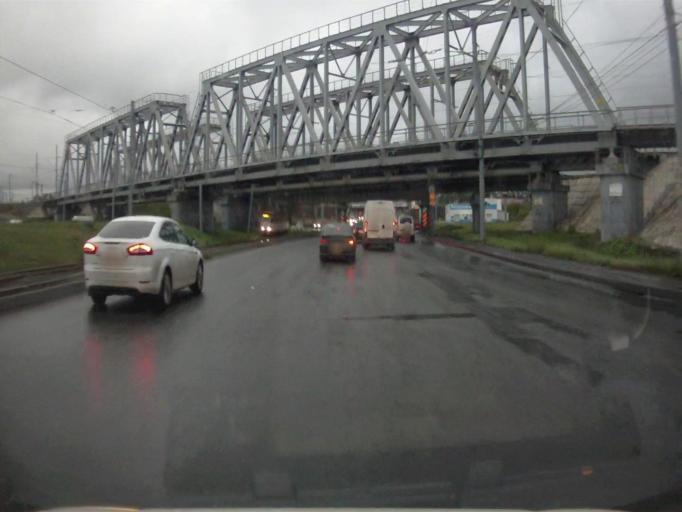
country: RU
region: Chelyabinsk
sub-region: Gorod Chelyabinsk
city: Chelyabinsk
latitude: 55.1548
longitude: 61.4431
